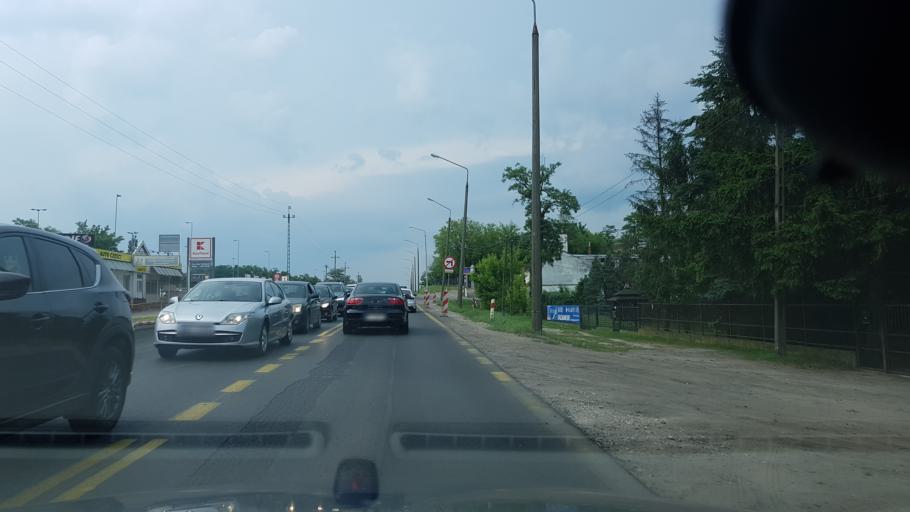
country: PL
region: Masovian Voivodeship
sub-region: Powiat legionowski
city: Michalow-Reginow
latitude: 52.4069
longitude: 20.9532
